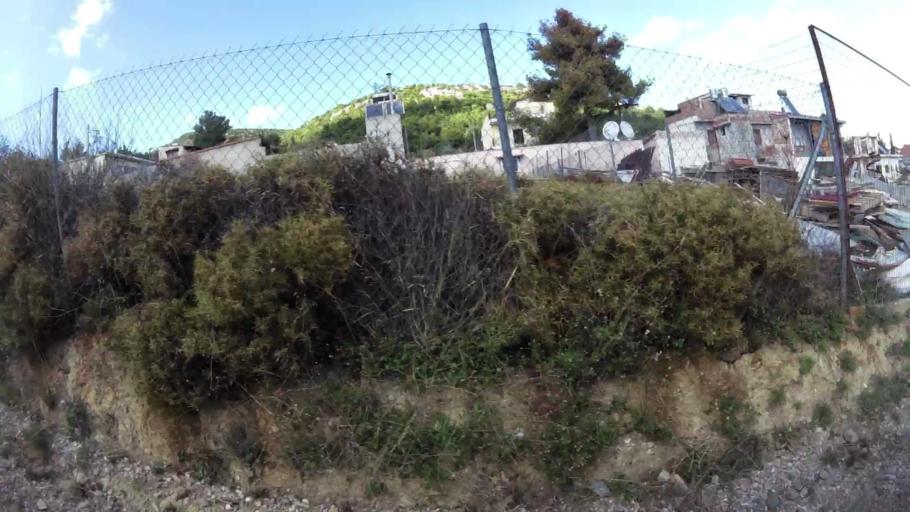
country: GR
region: Attica
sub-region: Nomarchia Anatolikis Attikis
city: Thrakomakedones
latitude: 38.1177
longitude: 23.7246
